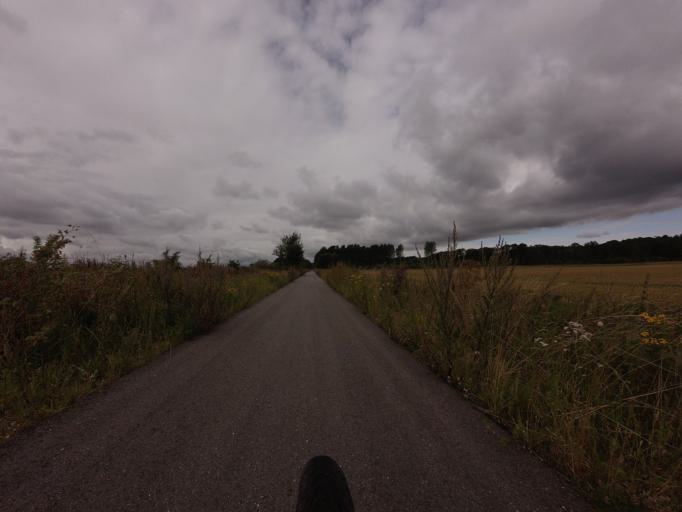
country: DK
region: Central Jutland
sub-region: Syddjurs Kommune
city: Ryomgard
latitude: 56.3835
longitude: 10.4724
